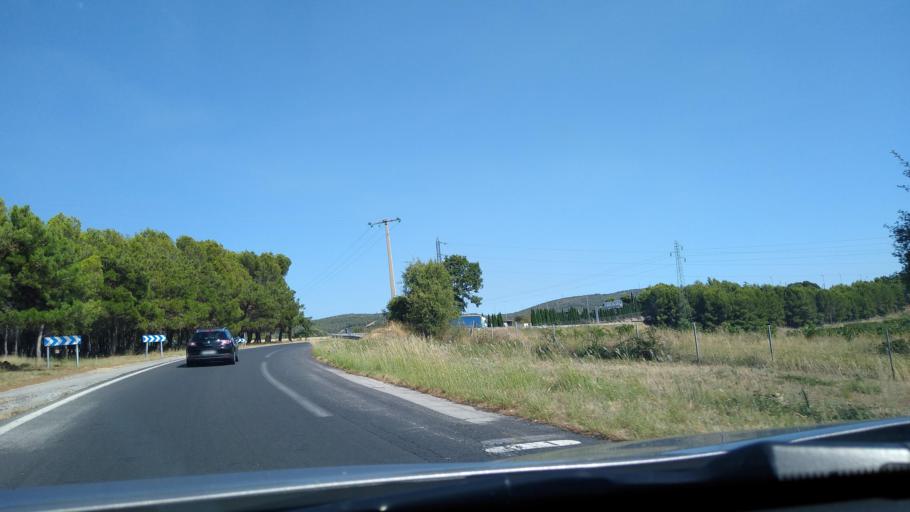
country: FR
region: Languedoc-Roussillon
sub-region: Departement de l'Herault
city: Poussan
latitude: 43.4805
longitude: 3.6823
